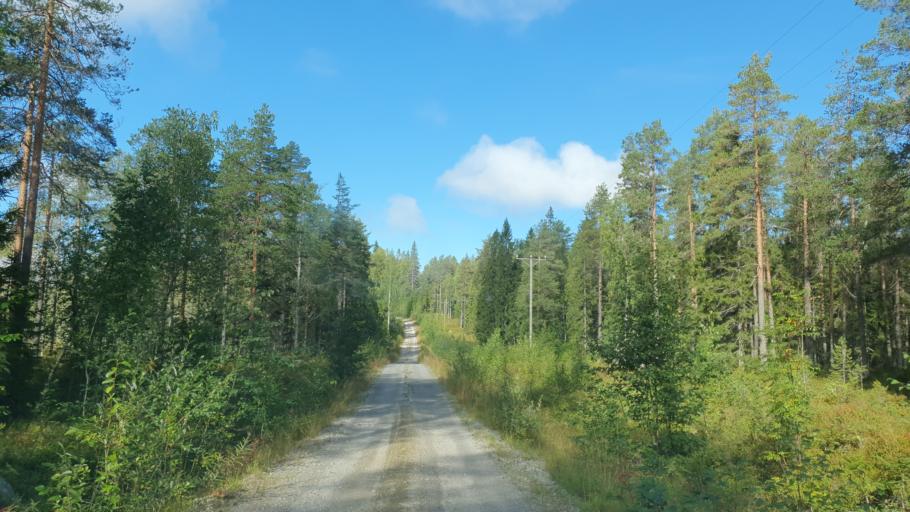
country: FI
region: Kainuu
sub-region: Kehys-Kainuu
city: Kuhmo
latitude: 64.0387
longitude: 29.1398
